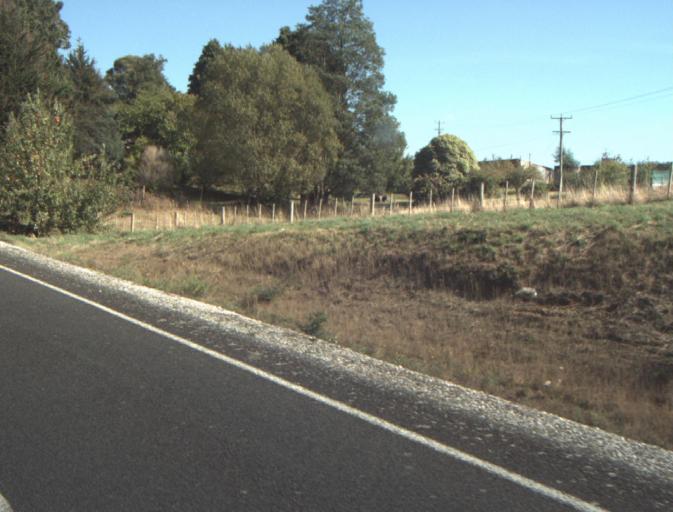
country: AU
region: Tasmania
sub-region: Launceston
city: Mayfield
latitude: -41.2830
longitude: 147.2186
